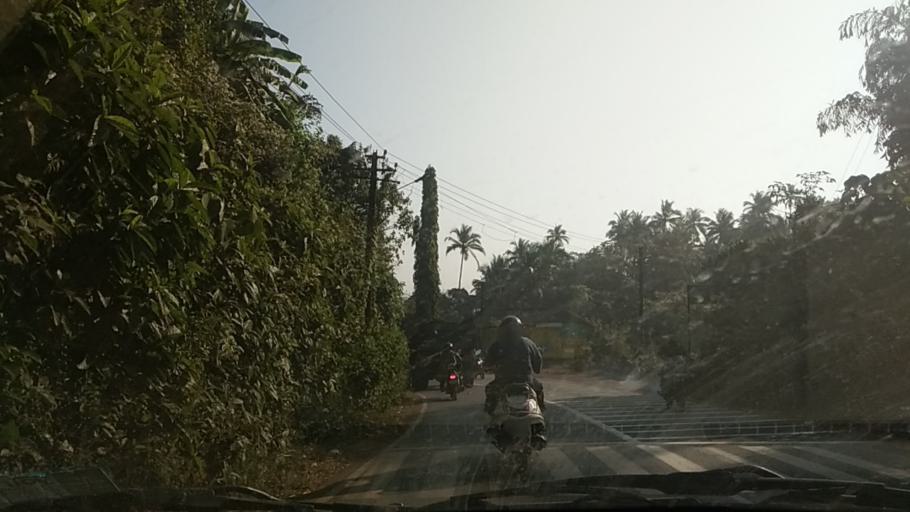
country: IN
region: Goa
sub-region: South Goa
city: Sanvordem
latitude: 15.2725
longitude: 74.1200
